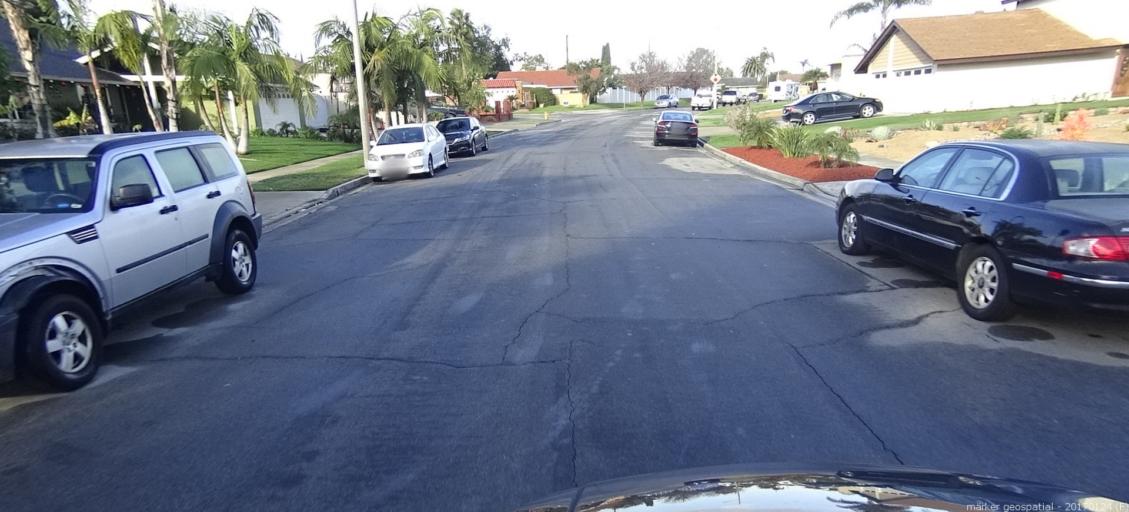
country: US
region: California
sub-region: Orange County
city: Laguna Hills
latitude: 33.6111
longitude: -117.6943
